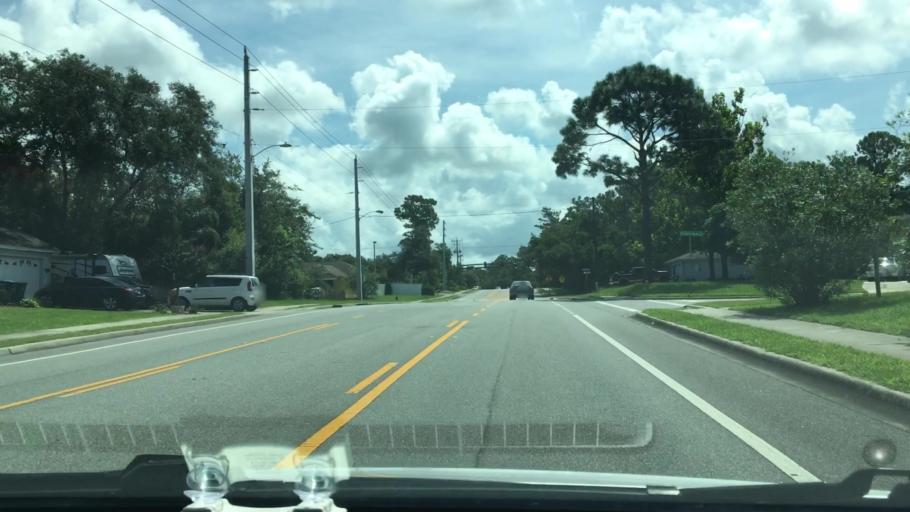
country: US
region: Florida
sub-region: Volusia County
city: Deltona
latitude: 28.8782
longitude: -81.1811
